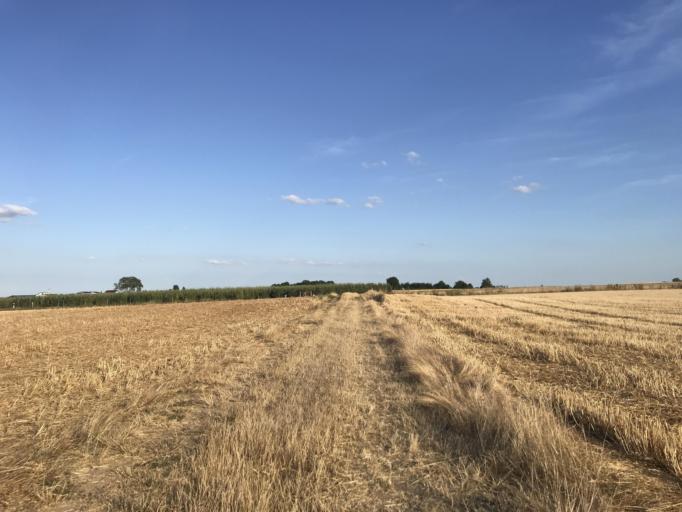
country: DE
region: Rheinland-Pfalz
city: Ober-Olm
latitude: 49.9462
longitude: 8.1795
